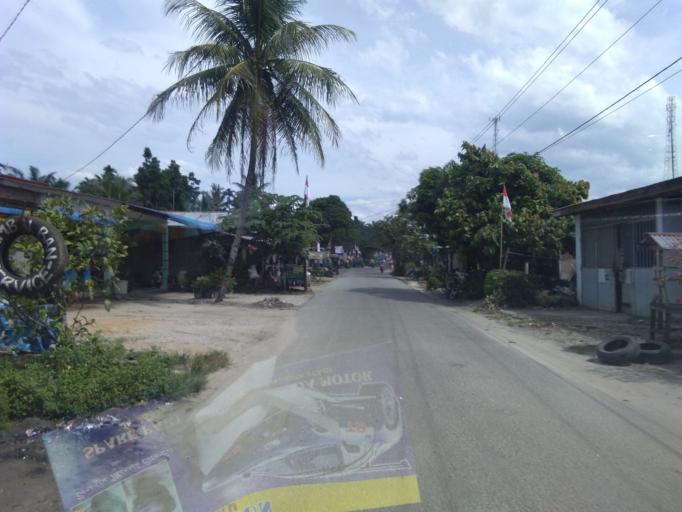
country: ID
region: North Sumatra
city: Deli Tua
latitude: 3.3009
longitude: 98.8081
